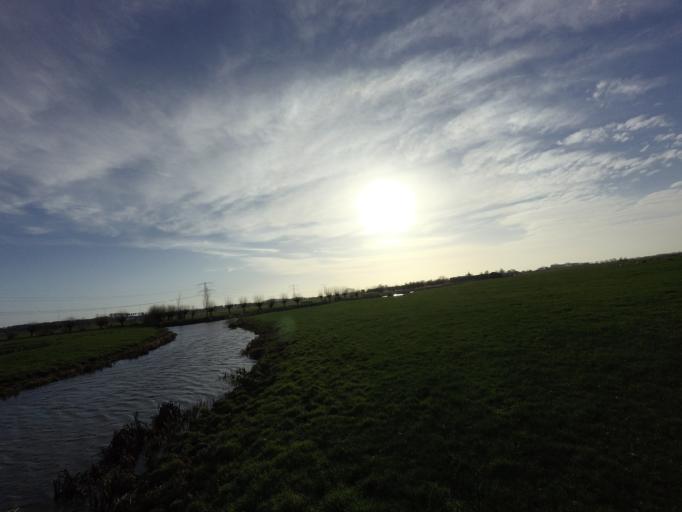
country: NL
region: Utrecht
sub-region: Stichtse Vecht
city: Breukelen
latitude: 52.1989
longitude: 4.9811
